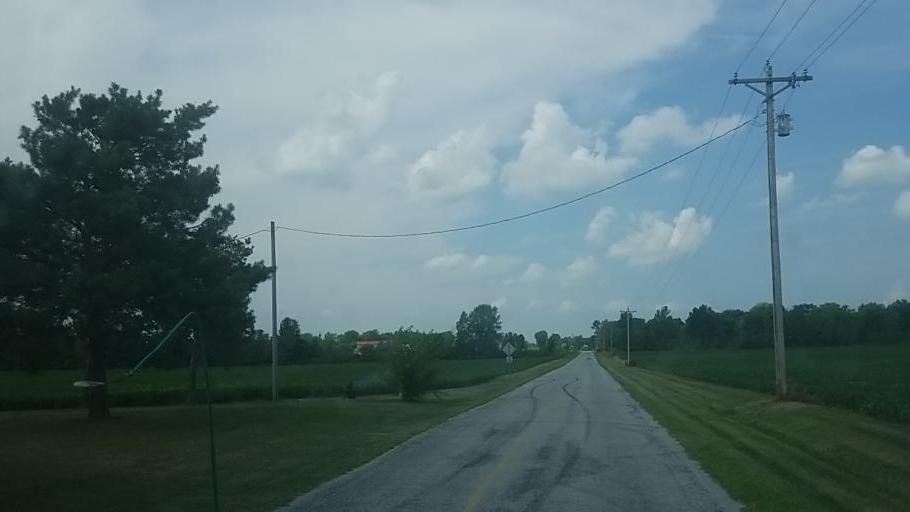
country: US
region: Ohio
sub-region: Hardin County
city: Kenton
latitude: 40.7405
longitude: -83.6015
